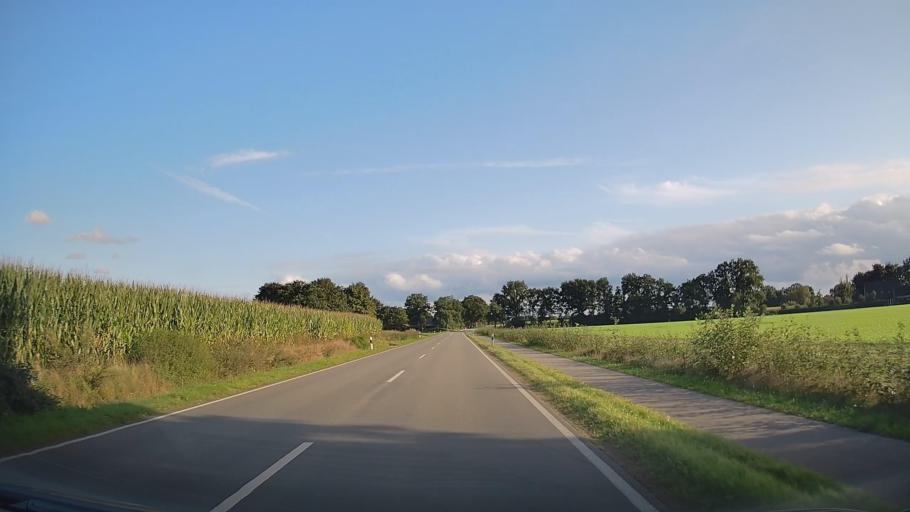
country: DE
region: Lower Saxony
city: Hilkenbrook
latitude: 53.0702
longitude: 7.7199
